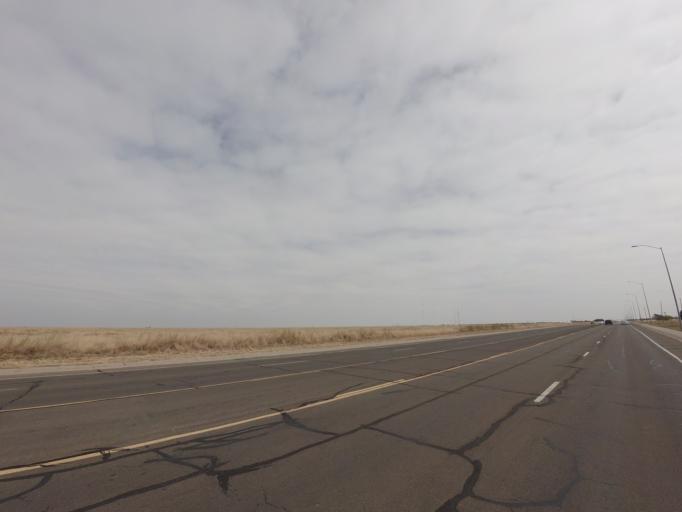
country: US
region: New Mexico
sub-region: Curry County
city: Clovis
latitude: 34.4340
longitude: -103.2262
